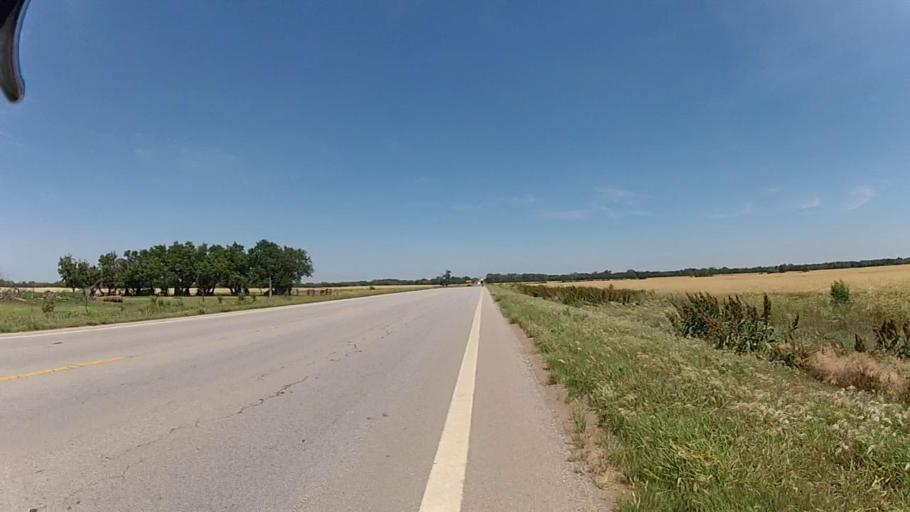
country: US
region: Kansas
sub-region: Harper County
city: Harper
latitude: 37.2387
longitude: -98.1084
